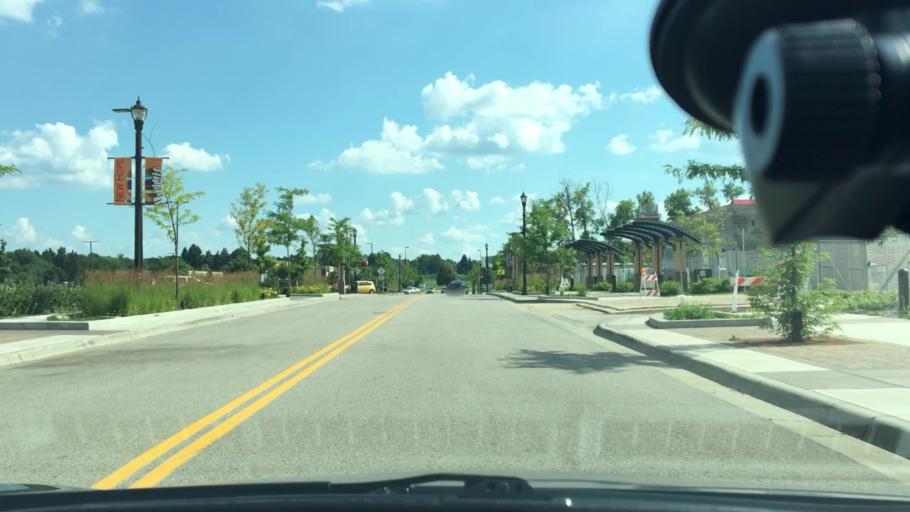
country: US
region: Minnesota
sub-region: Hennepin County
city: New Hope
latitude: 45.0352
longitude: -93.3854
